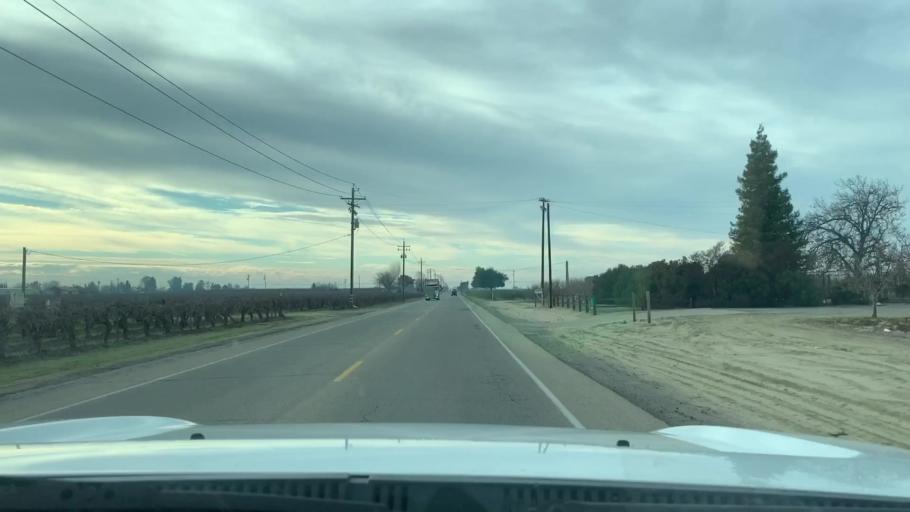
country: US
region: California
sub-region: Fresno County
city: Fowler
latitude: 36.6055
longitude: -119.6765
